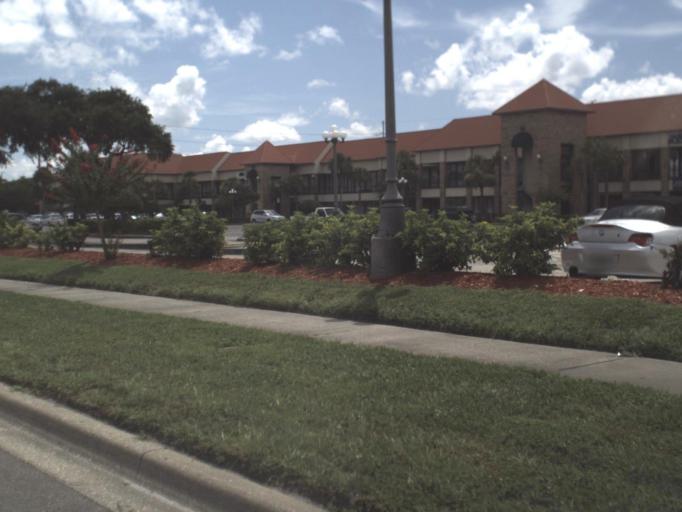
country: US
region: Florida
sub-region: Hillsborough County
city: Egypt Lake-Leto
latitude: 28.0093
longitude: -82.5052
